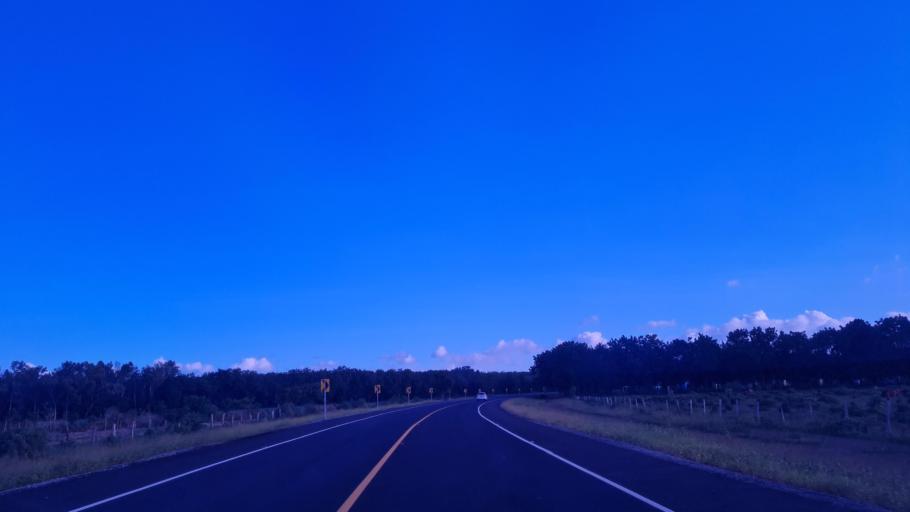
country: NI
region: Masaya
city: Ticuantepe
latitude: 12.0983
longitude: -86.1592
